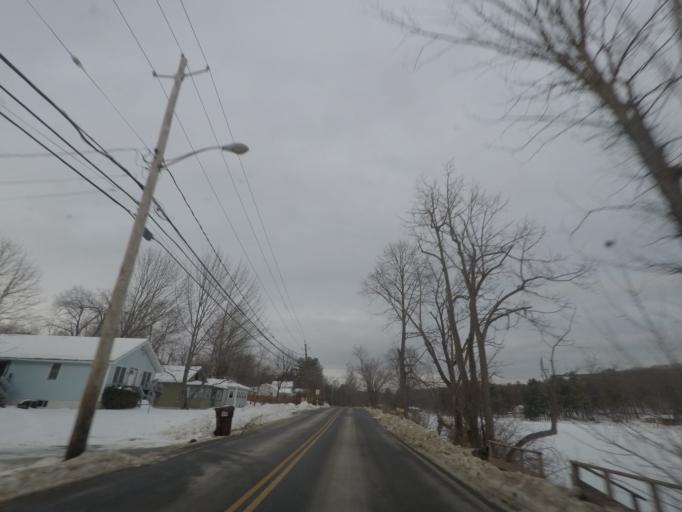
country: US
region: New York
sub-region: Rensselaer County
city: Averill Park
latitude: 42.6175
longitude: -73.5680
